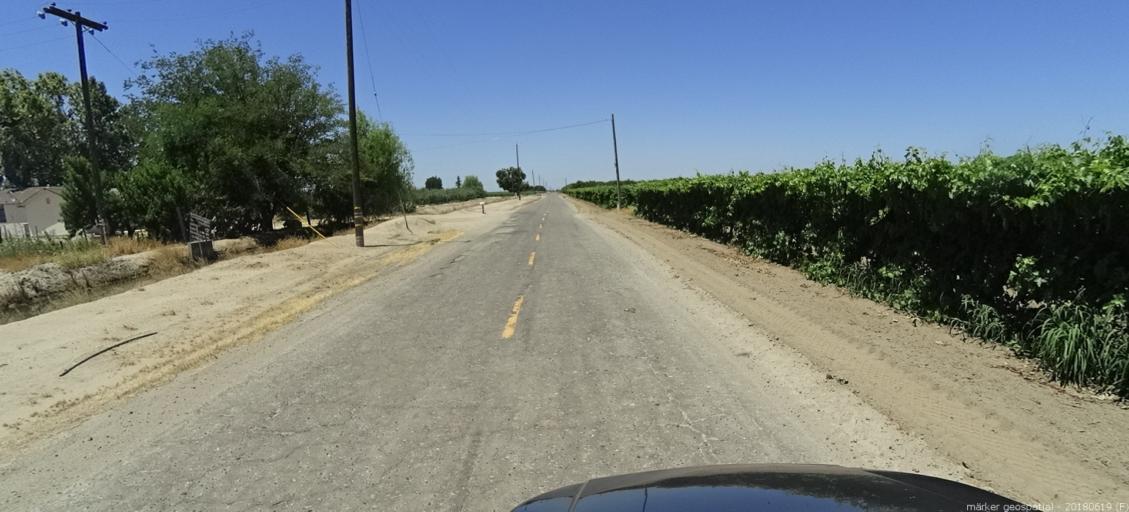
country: US
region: California
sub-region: Madera County
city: Parkwood
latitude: 36.8731
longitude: -120.0806
